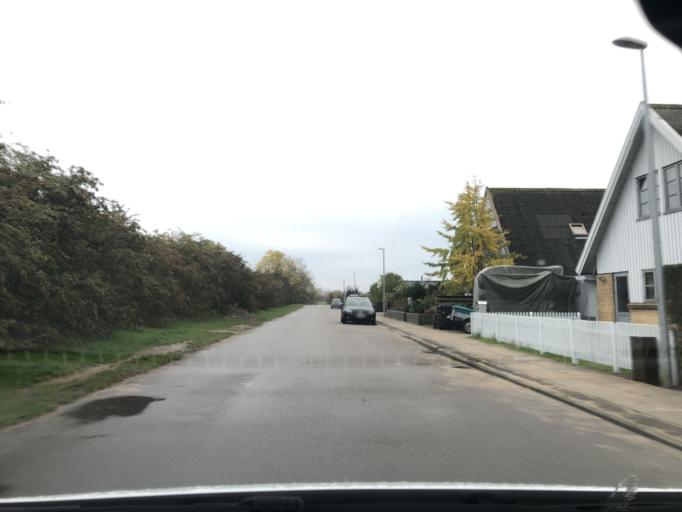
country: DK
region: Capital Region
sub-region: Tarnby Kommune
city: Tarnby
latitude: 55.5935
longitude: 12.5904
